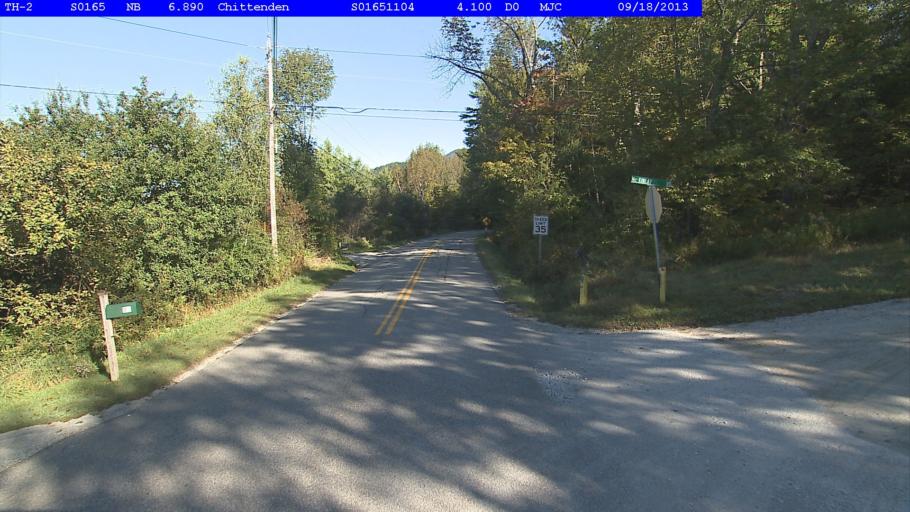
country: US
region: Vermont
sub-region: Rutland County
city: Rutland
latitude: 43.7331
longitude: -72.9712
